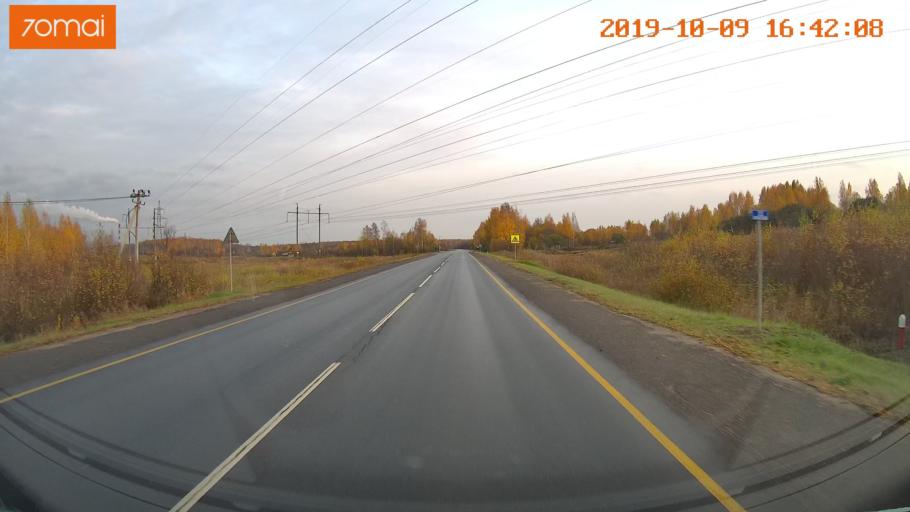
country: RU
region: Kostroma
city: Volgorechensk
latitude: 57.4654
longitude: 41.0944
